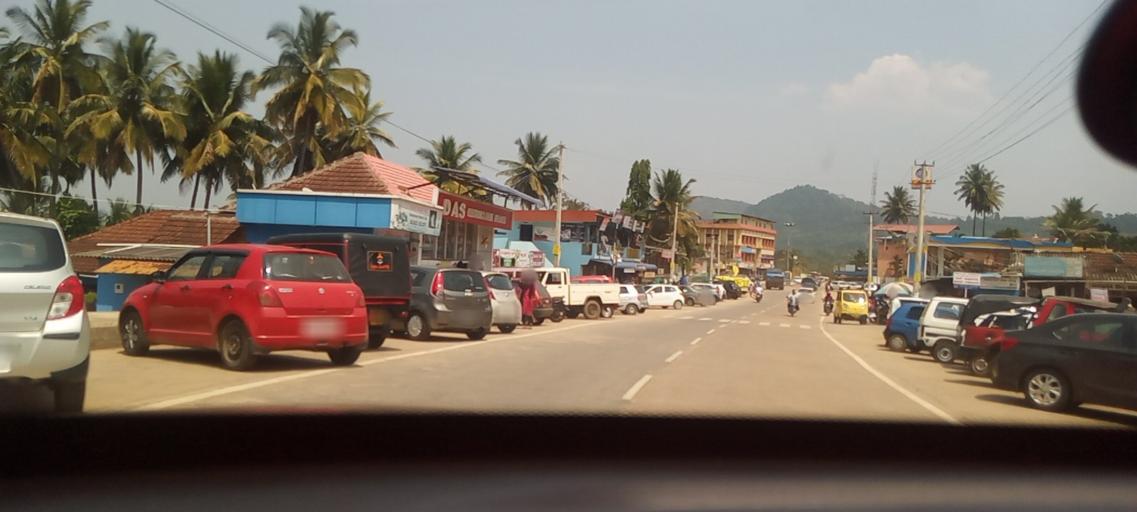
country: IN
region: Karnataka
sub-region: Chikmagalur
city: Koppa
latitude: 13.3506
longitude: 75.4645
